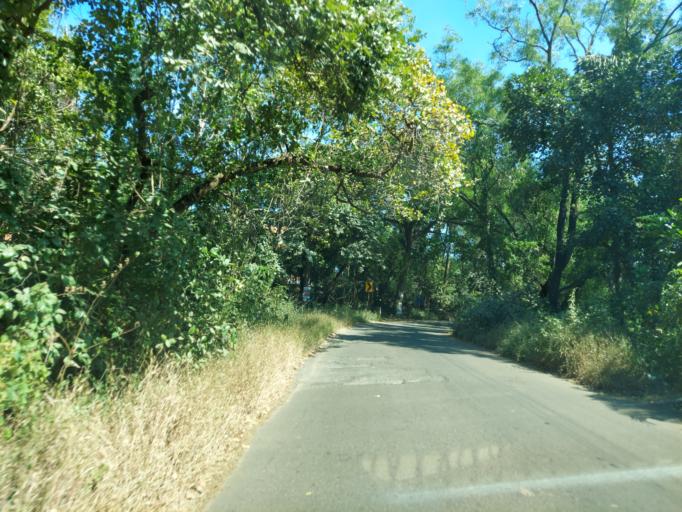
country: IN
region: Maharashtra
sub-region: Sindhudurg
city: Kudal
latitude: 15.9884
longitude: 73.6818
